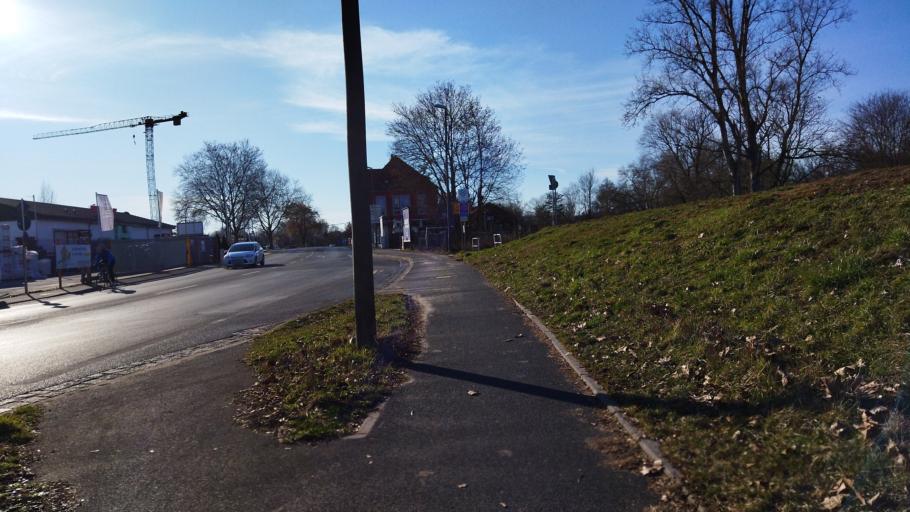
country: DE
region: Bavaria
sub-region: Regierungsbezirk Unterfranken
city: Sennfeld
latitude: 50.0391
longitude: 10.2426
